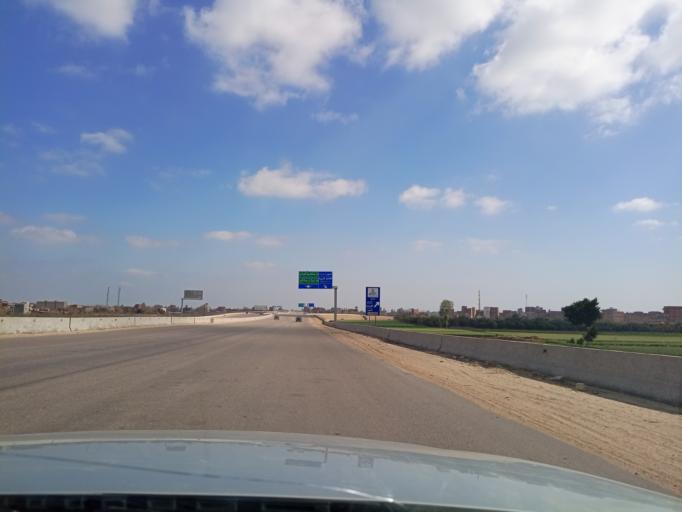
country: EG
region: Muhafazat al Minufiyah
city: Al Bajur
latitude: 30.4019
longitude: 31.0299
